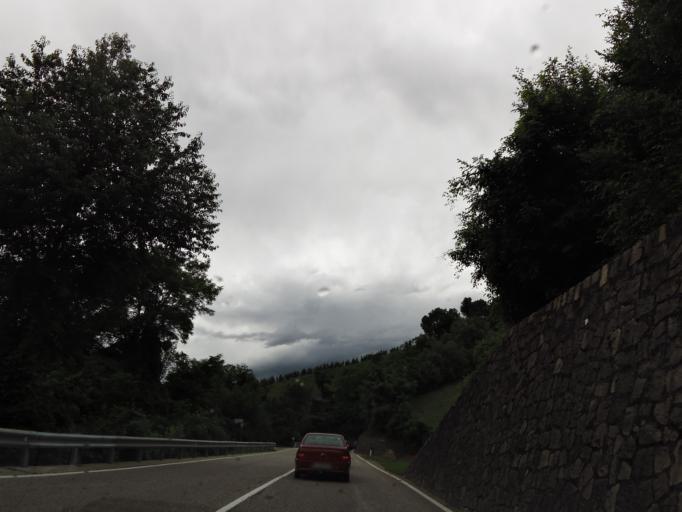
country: IT
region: Trentino-Alto Adige
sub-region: Bolzano
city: Fie Allo Sciliar
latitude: 46.5099
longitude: 11.5089
